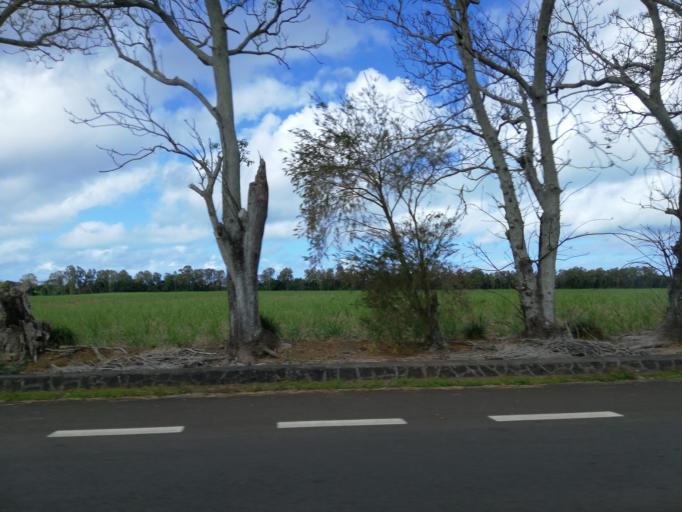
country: MU
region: Grand Port
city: Mahebourg
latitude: -20.3788
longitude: 57.6985
